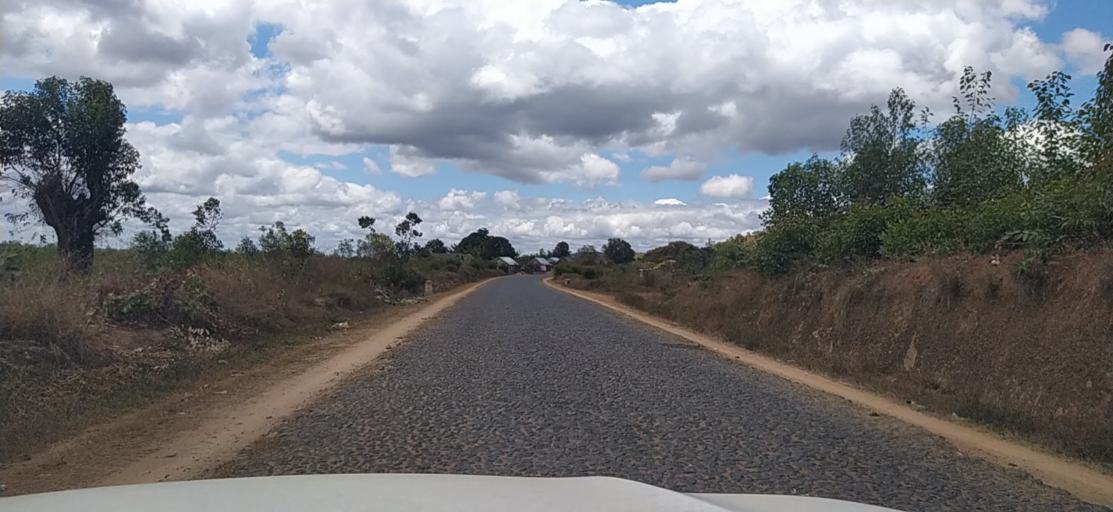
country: MG
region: Alaotra Mangoro
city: Moramanga
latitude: -18.7545
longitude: 48.2594
